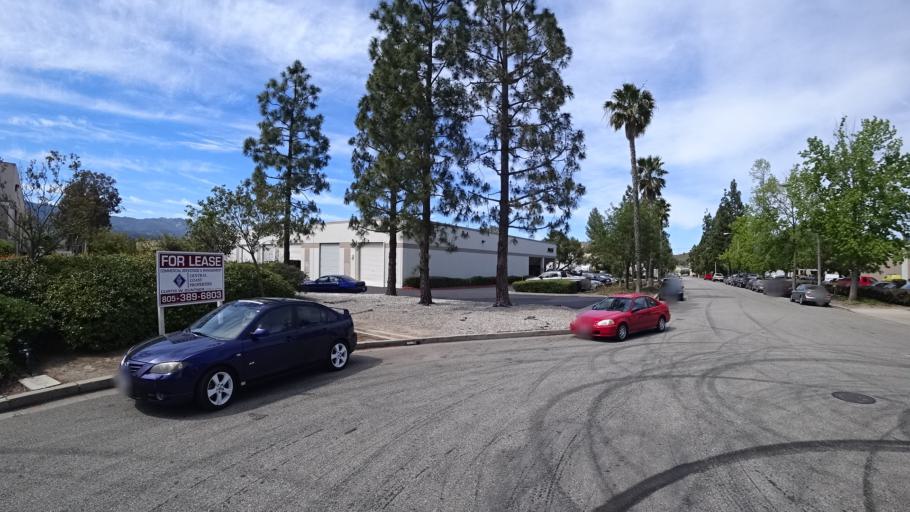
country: US
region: California
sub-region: Ventura County
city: Casa Conejo
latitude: 34.1942
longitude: -118.9265
